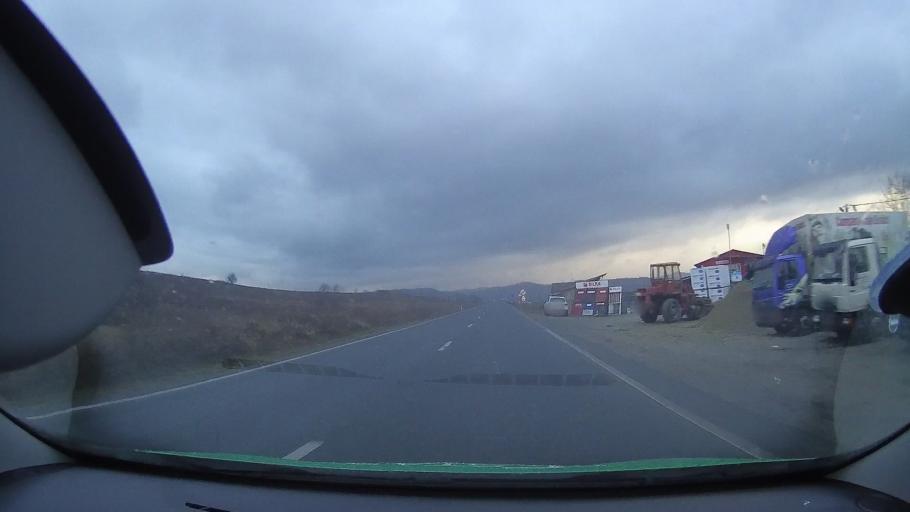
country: RO
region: Hunedoara
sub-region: Comuna Ribita
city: Ribita
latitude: 46.1577
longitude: 22.7633
